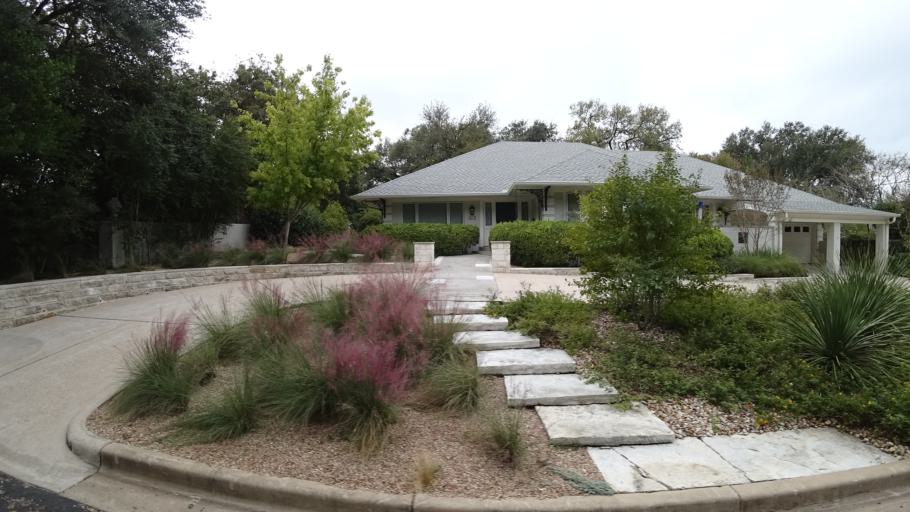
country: US
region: Texas
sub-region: Travis County
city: Austin
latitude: 30.2878
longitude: -97.7587
